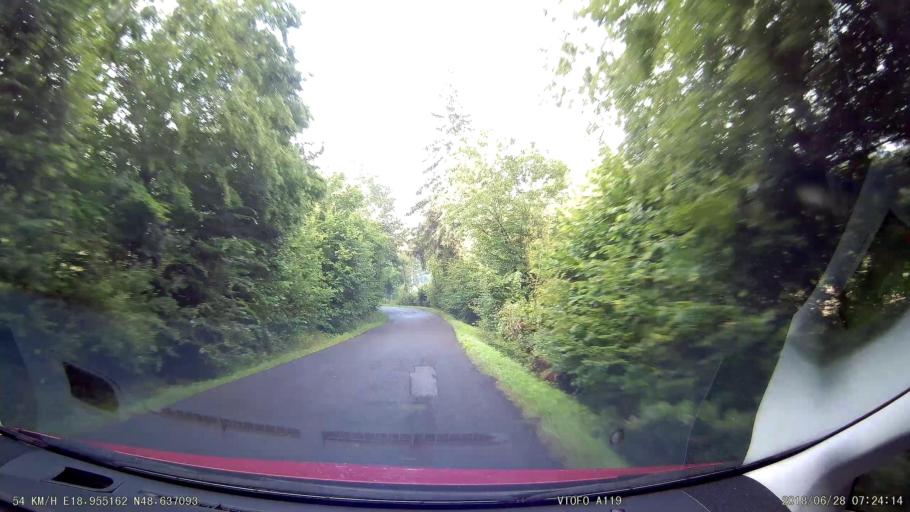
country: SK
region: Banskobystricky
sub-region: Okres Ziar nad Hronom
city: Kremnica
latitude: 48.6368
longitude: 18.9552
